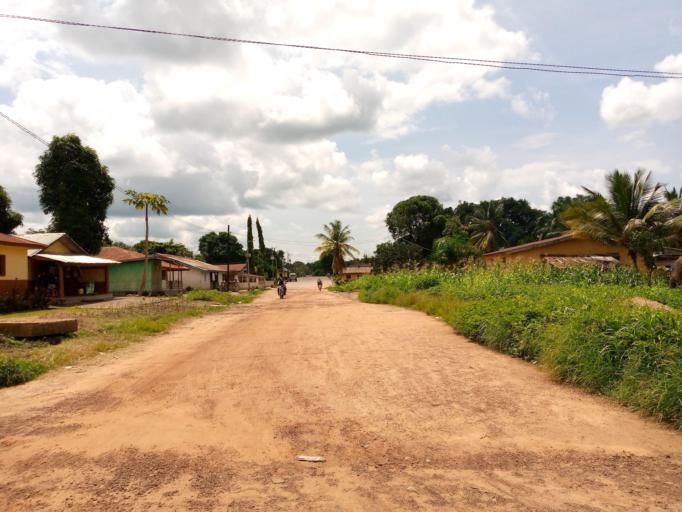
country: SL
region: Northern Province
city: Magburaka
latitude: 8.7139
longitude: -11.9362
